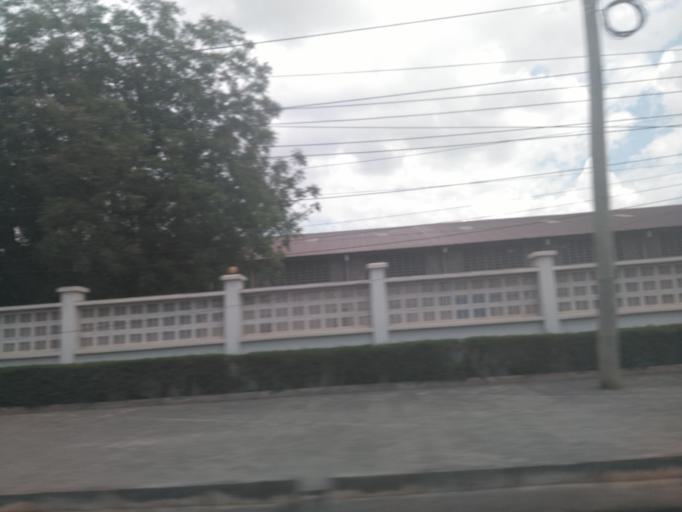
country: TZ
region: Dar es Salaam
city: Dar es Salaam
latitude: -6.8375
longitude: 39.2597
